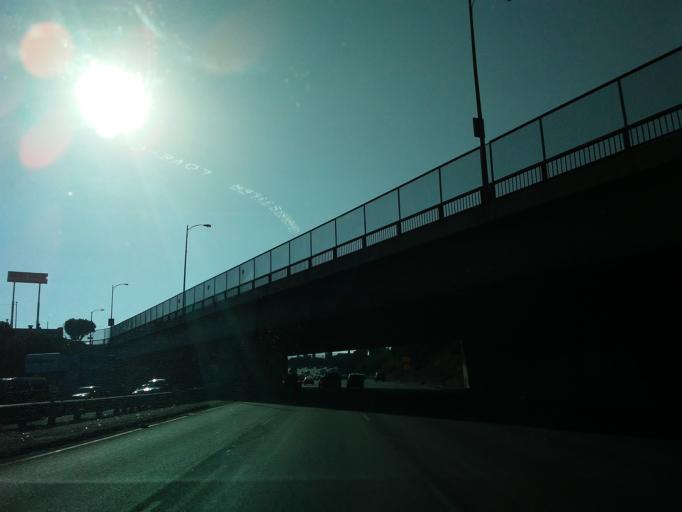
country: US
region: California
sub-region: Los Angeles County
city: East Los Angeles
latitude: 34.0187
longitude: -118.1777
